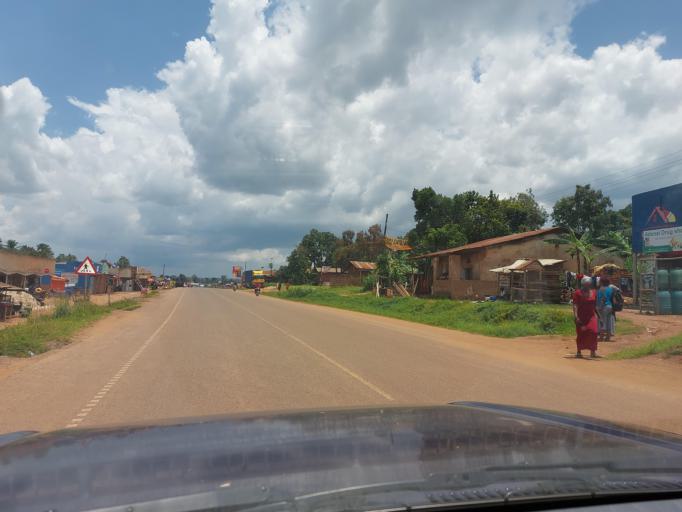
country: UG
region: Central Region
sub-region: Mukono District
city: Mukono
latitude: 0.3016
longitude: 32.7776
